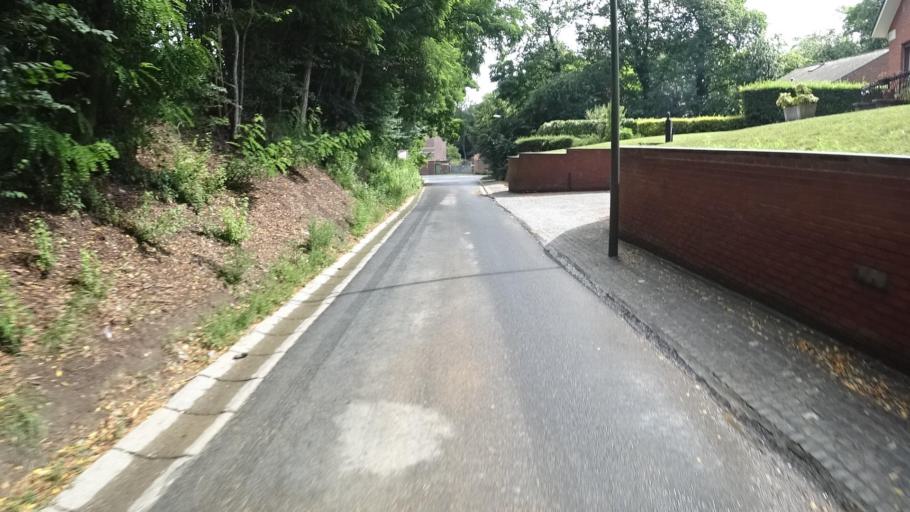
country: BE
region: Wallonia
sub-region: Province du Brabant Wallon
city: Villers-la-Ville
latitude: 50.5693
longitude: 4.4983
